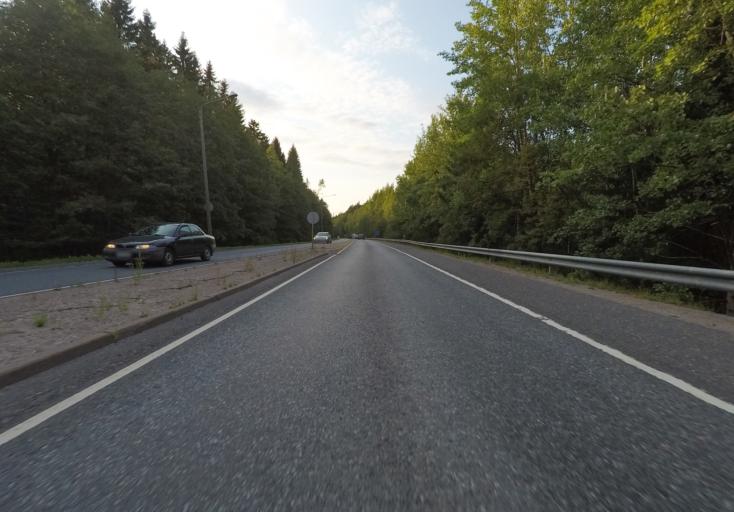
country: FI
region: Paijanne Tavastia
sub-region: Lahti
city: Lahti
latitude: 60.9912
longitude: 25.7300
